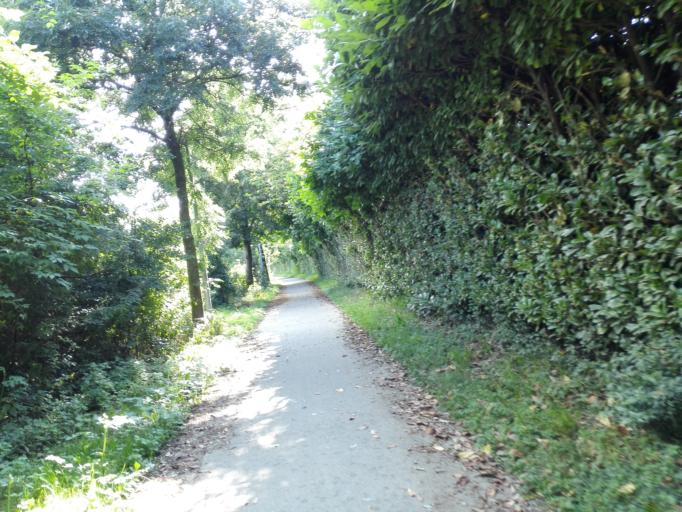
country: BE
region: Flanders
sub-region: Provincie Vlaams-Brabant
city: Tienen
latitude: 50.8032
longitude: 4.9708
